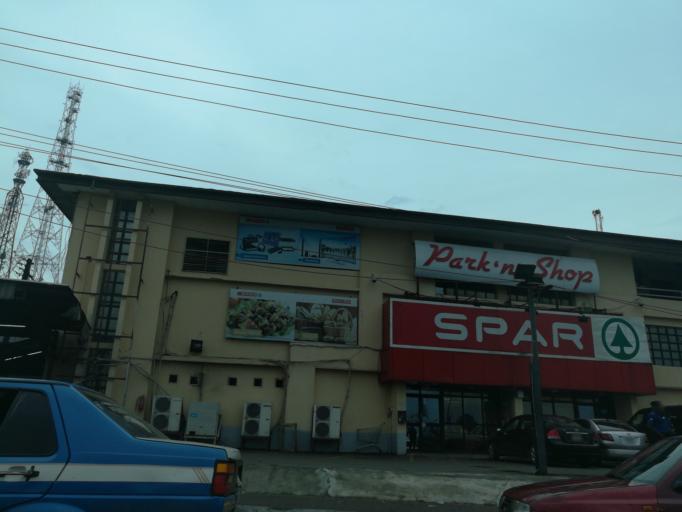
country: NG
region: Rivers
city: Port Harcourt
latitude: 4.8059
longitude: 7.0089
